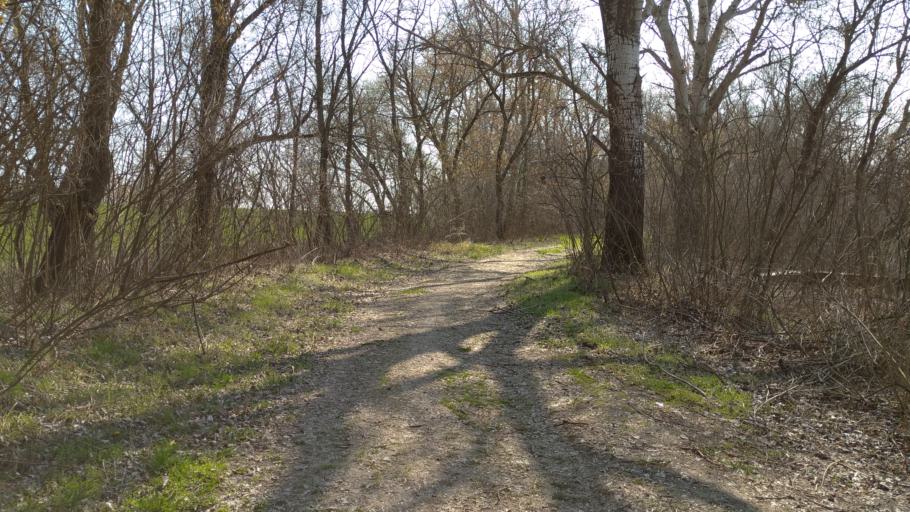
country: HU
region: Csongrad
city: Mindszent
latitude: 46.4858
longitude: 20.2169
